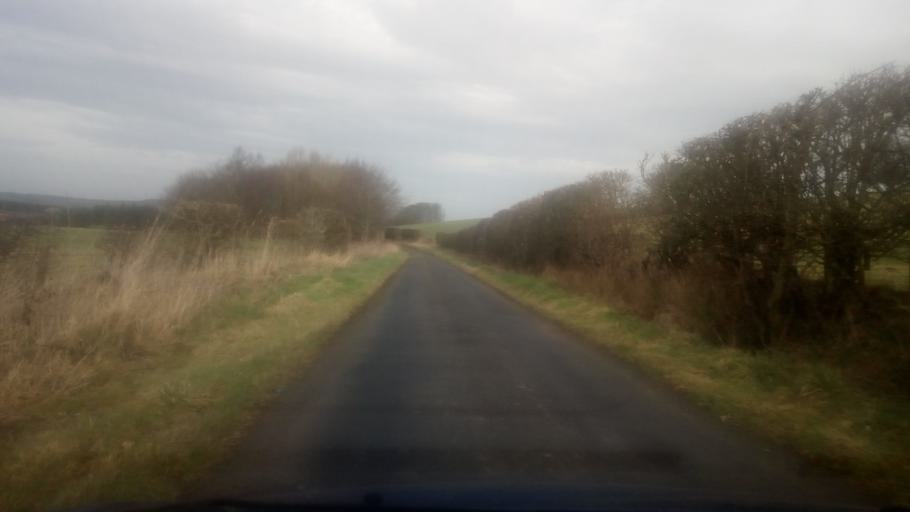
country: GB
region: Scotland
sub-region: The Scottish Borders
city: Jedburgh
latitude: 55.4423
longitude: -2.6308
